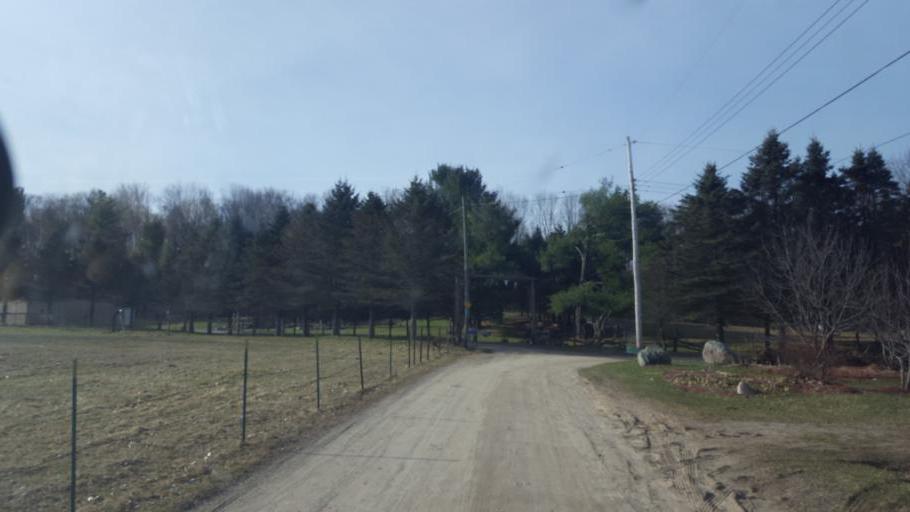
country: US
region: Michigan
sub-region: Montcalm County
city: Howard City
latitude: 43.4886
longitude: -85.4321
